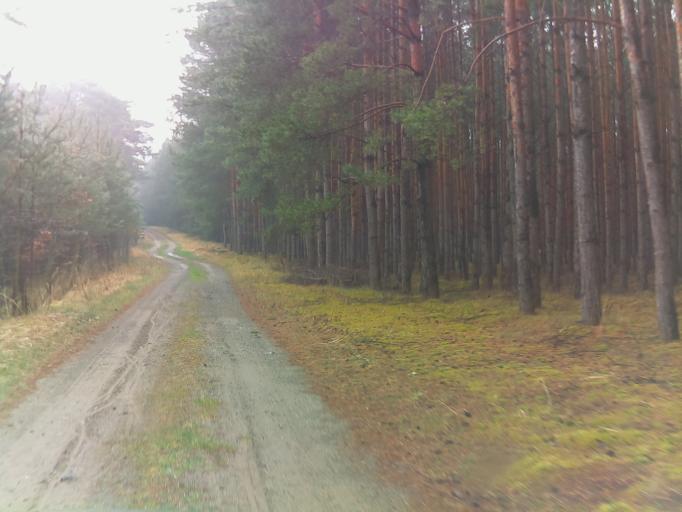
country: DE
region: Brandenburg
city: Lieberose
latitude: 52.0257
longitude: 14.2315
